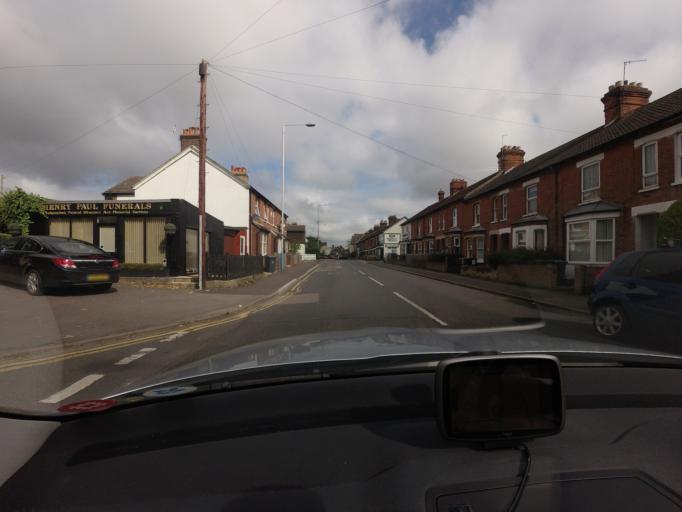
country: GB
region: England
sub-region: Kent
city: Tonbridge
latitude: 51.2057
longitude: 0.2774
